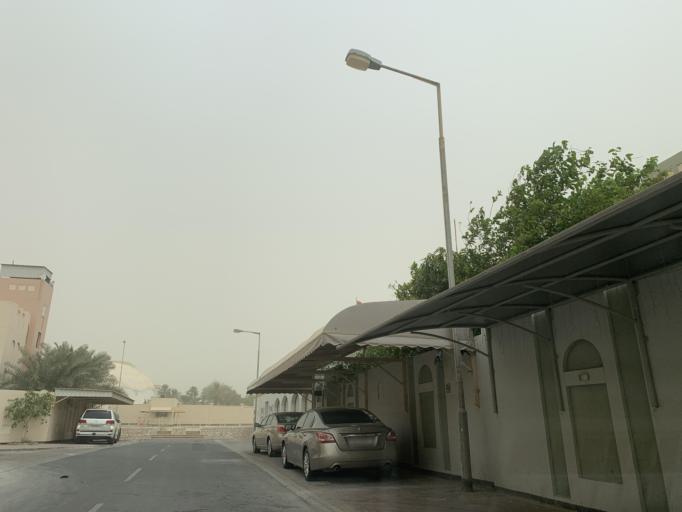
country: BH
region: Central Governorate
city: Madinat Hamad
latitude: 26.1366
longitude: 50.5136
